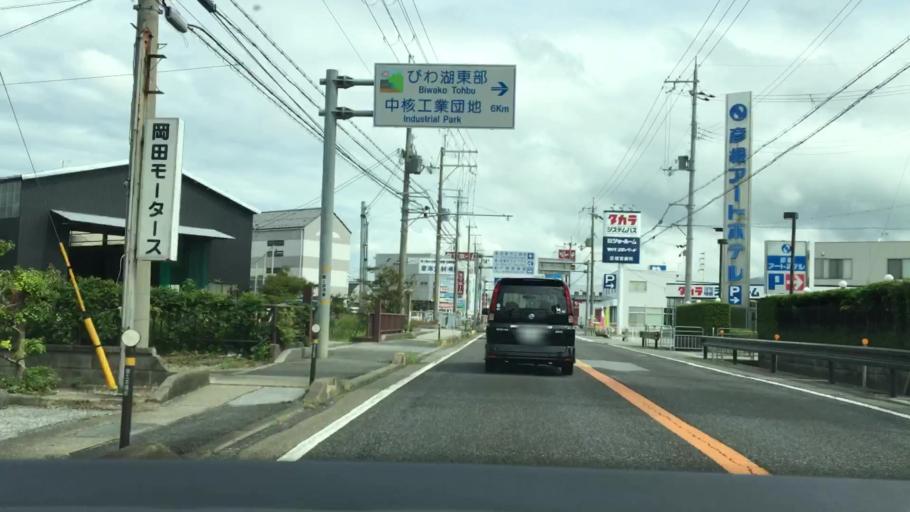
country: JP
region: Shiga Prefecture
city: Hikone
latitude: 35.2394
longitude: 136.2548
